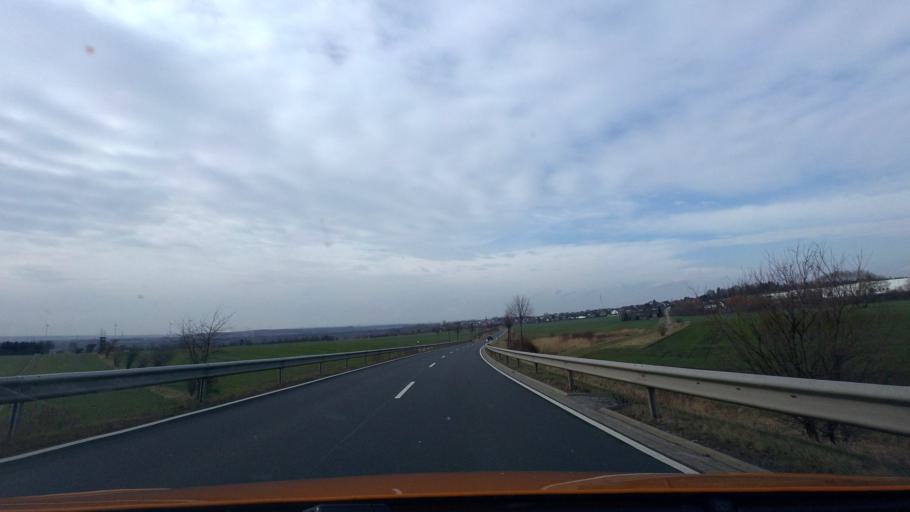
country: DE
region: Lower Saxony
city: Helmstedt
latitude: 52.2123
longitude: 11.0321
